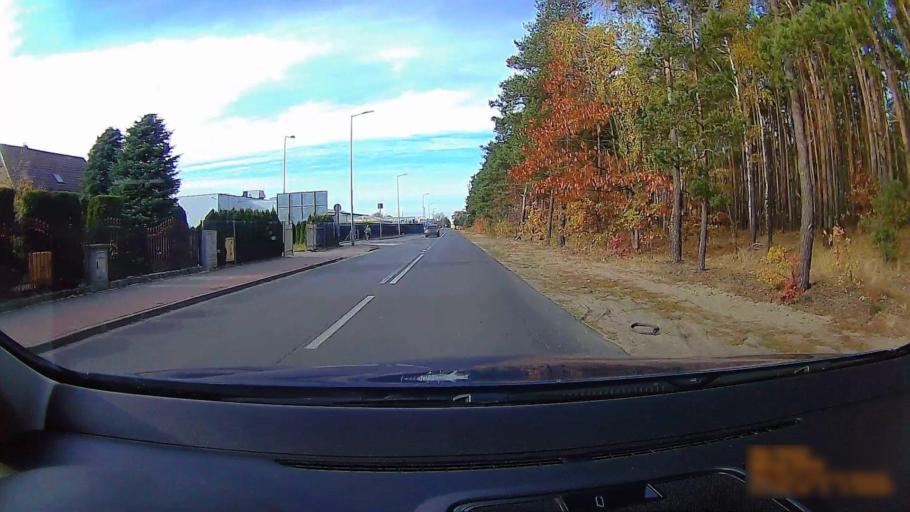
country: PL
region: Greater Poland Voivodeship
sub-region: Powiat ostrzeszowski
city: Ostrzeszow
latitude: 51.4354
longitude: 17.9190
